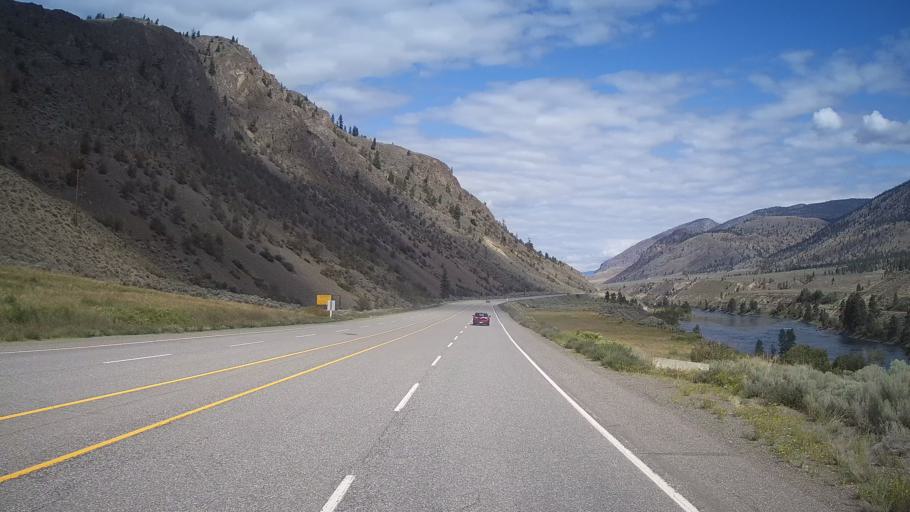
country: CA
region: British Columbia
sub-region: Thompson-Nicola Regional District
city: Ashcroft
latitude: 50.5195
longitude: -121.2843
